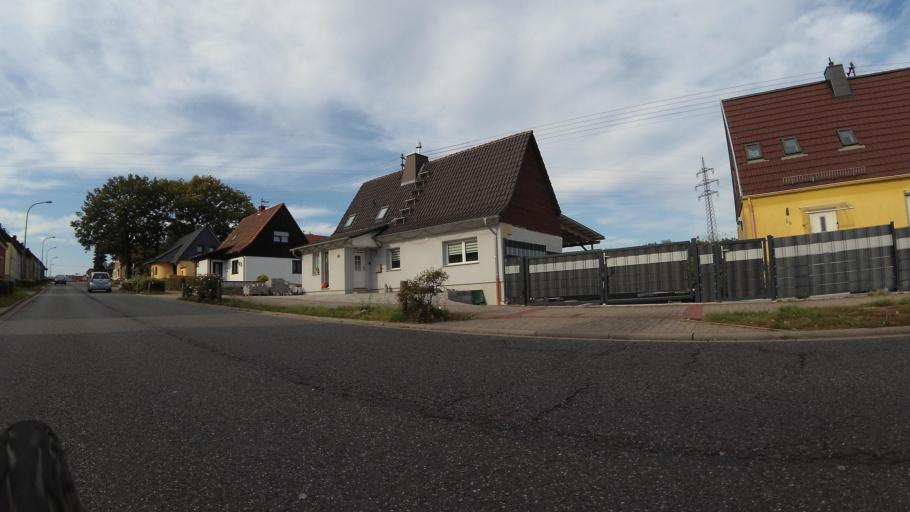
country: DE
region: Saarland
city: Friedrichsthal
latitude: 49.3326
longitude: 7.0874
